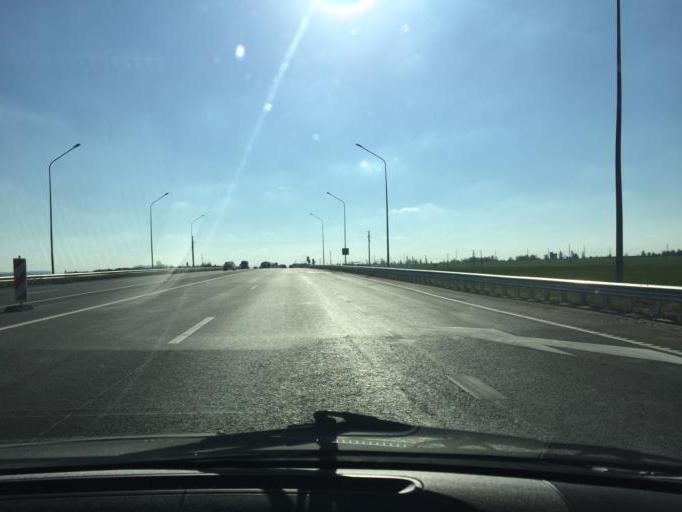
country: BY
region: Minsk
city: Slutsk
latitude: 52.9912
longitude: 27.5073
